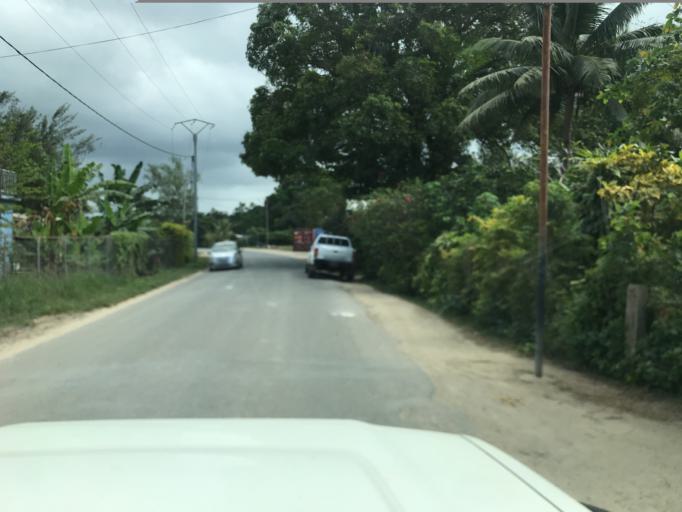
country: VU
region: Sanma
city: Luganville
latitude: -15.5124
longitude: 167.1714
